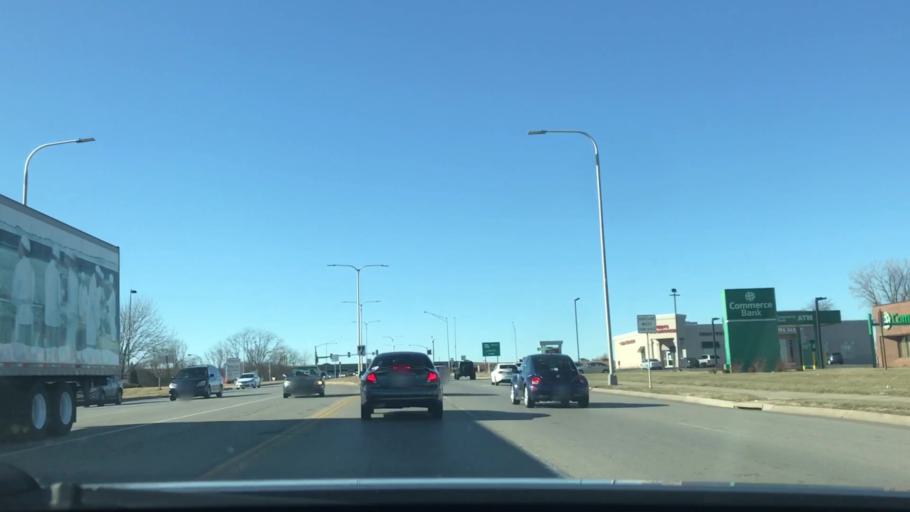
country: US
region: Missouri
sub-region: Jackson County
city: East Independence
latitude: 39.0481
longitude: -94.3600
